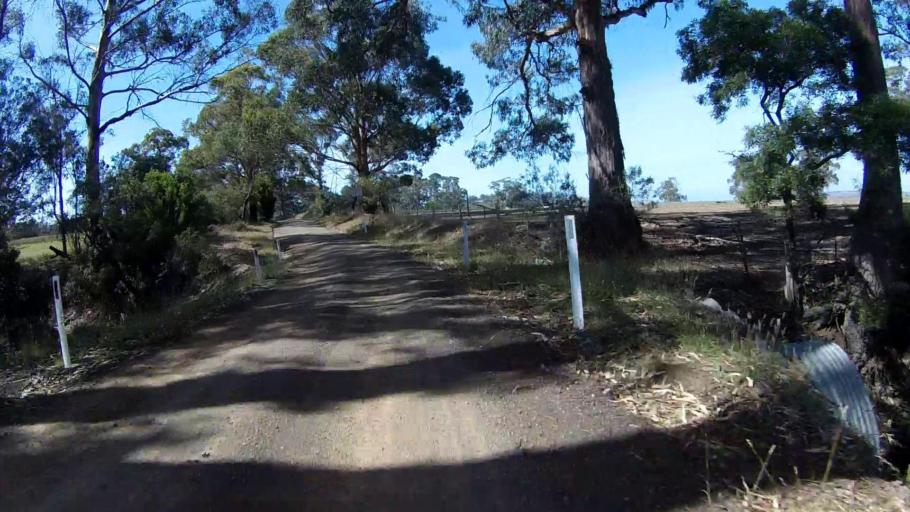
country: AU
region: Tasmania
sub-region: Sorell
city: Sorell
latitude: -42.7228
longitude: 147.5952
